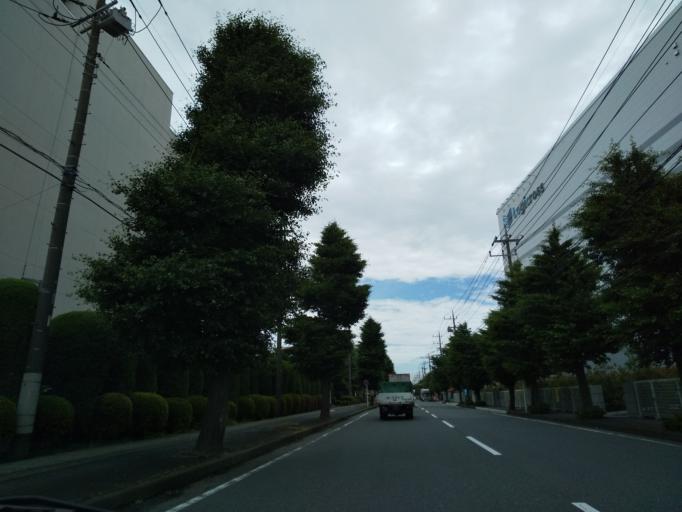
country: JP
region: Kanagawa
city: Zama
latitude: 35.5142
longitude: 139.3567
